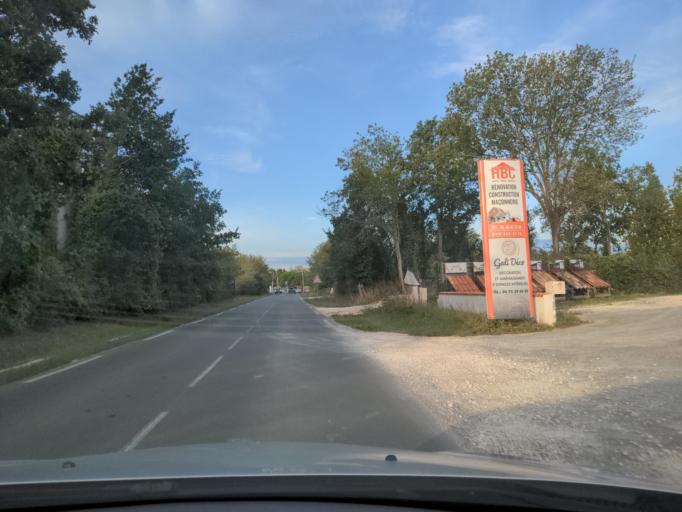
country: FR
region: Poitou-Charentes
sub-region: Departement de la Charente-Maritime
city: Saint-Trojan-les-Bains
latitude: 45.8795
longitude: -1.2168
